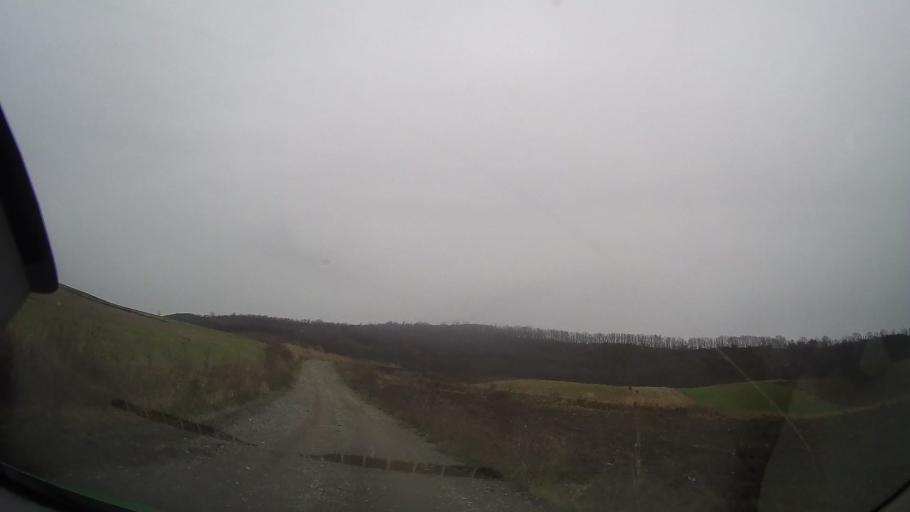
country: RO
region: Mures
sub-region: Comuna Ceausu de Campie
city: Ceausu de Campie
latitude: 46.6493
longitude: 24.4976
